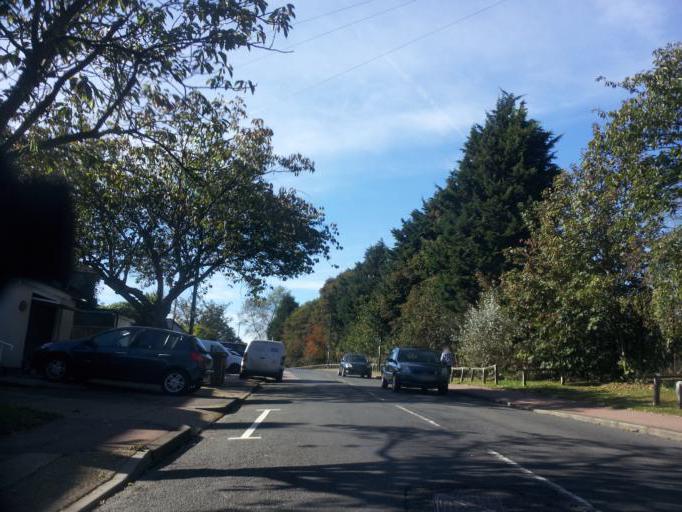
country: GB
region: England
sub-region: Kent
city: Chatham
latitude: 51.3655
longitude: 0.5379
